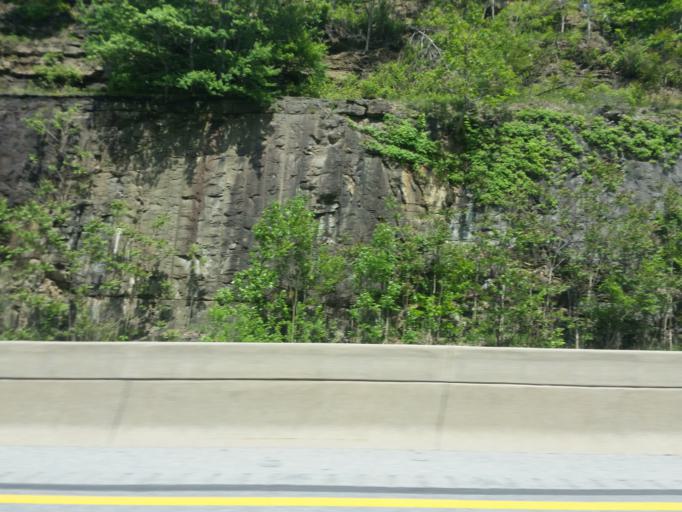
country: US
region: West Virginia
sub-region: Fayette County
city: Oak Hill
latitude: 37.9919
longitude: -81.3342
